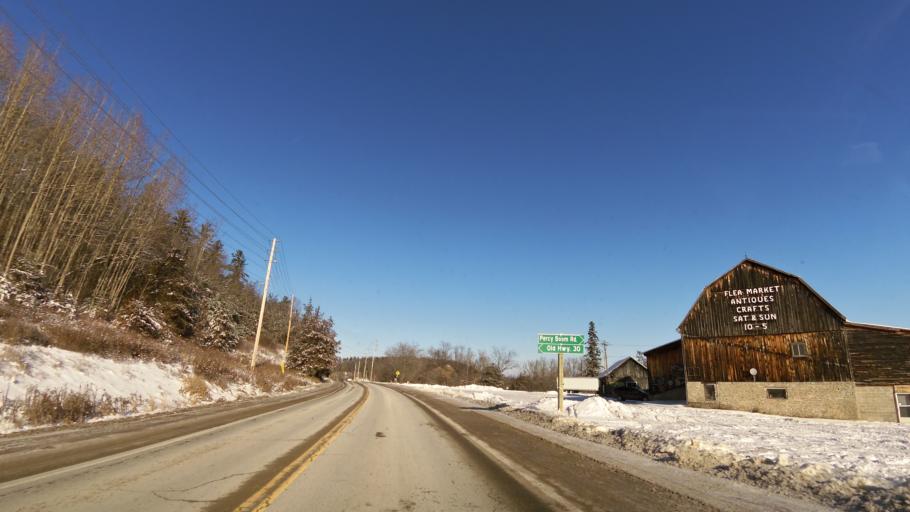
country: CA
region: Ontario
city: Quinte West
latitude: 44.2468
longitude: -77.8164
